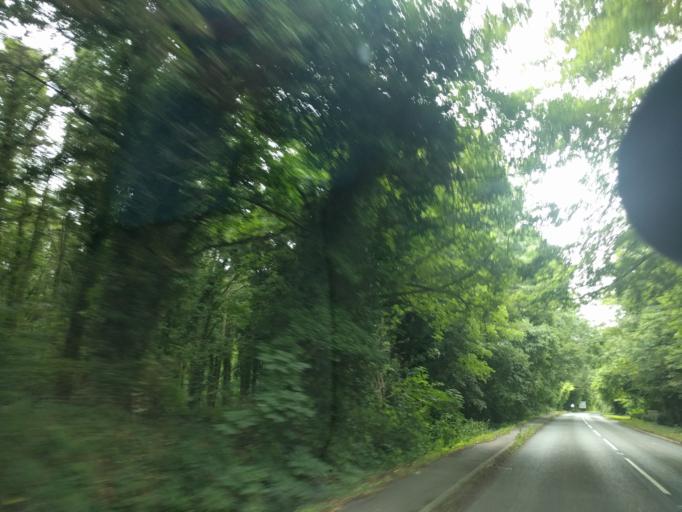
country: GB
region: England
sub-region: Wiltshire
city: Erlestoke
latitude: 51.2825
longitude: -2.0384
